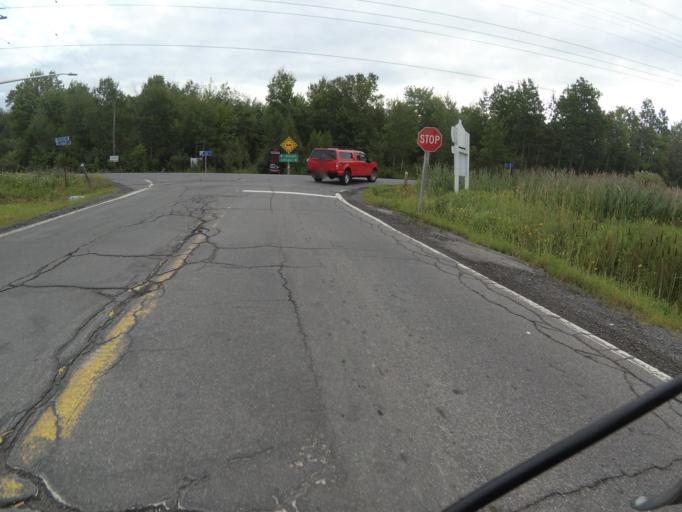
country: CA
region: Ontario
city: Bourget
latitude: 45.3528
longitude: -75.2797
